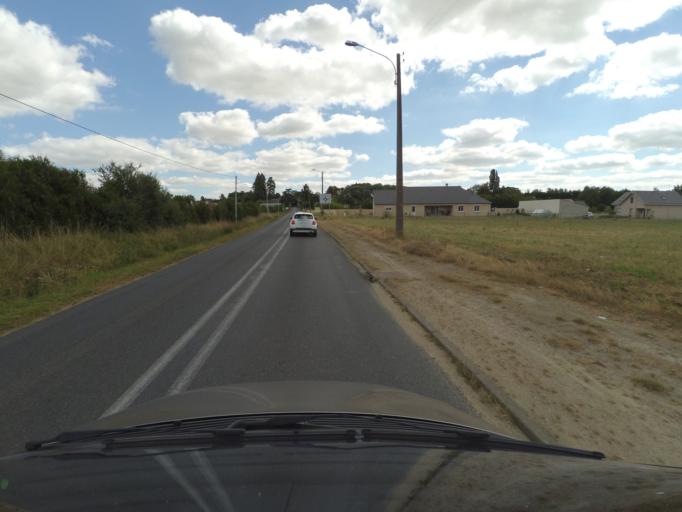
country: FR
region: Pays de la Loire
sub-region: Departement de Maine-et-Loire
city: Doue-la-Fontaine
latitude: 47.2009
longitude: -0.2758
